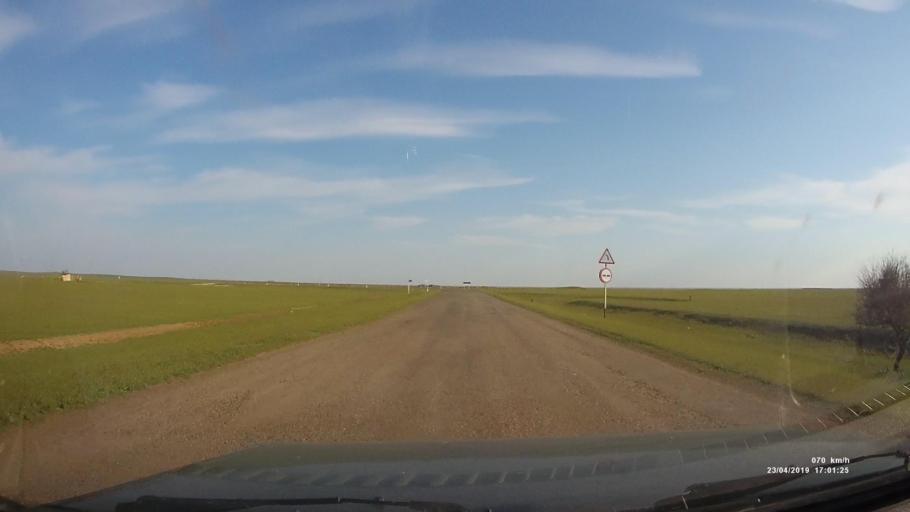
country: RU
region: Kalmykiya
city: Priyutnoye
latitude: 46.2962
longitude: 43.4079
